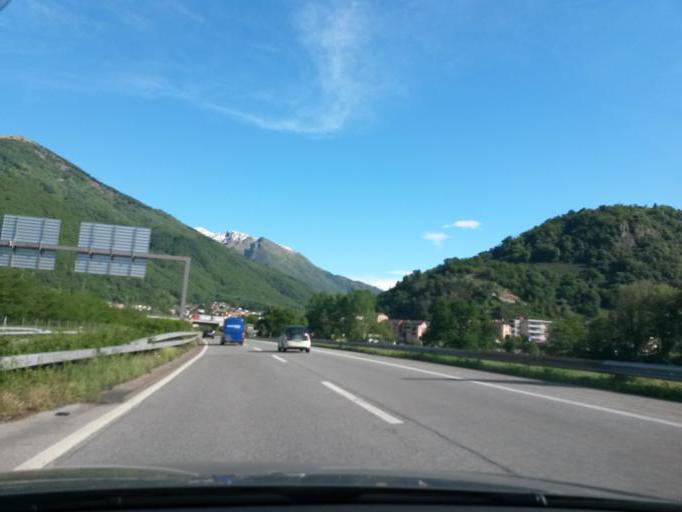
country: CH
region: Ticino
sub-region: Lugano District
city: Cadempino
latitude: 46.0406
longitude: 8.9285
